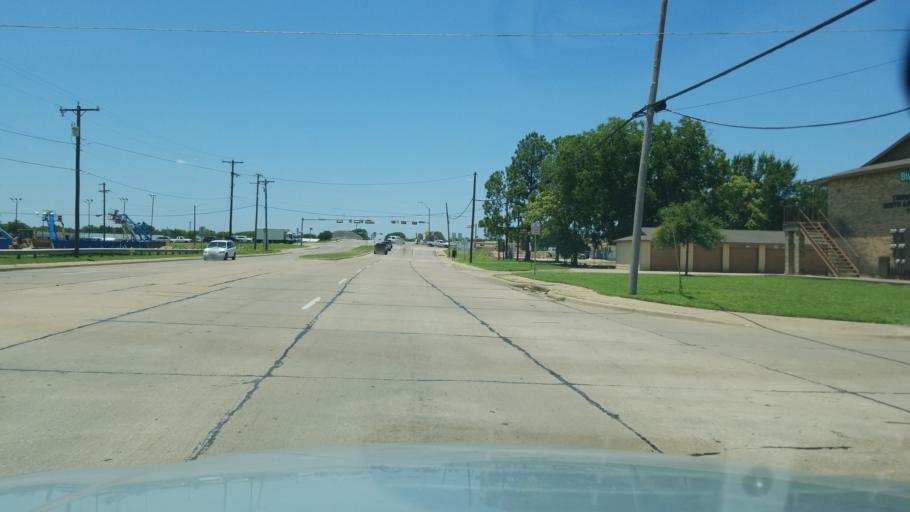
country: US
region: Texas
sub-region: Dallas County
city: Irving
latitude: 32.8013
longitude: -96.9191
